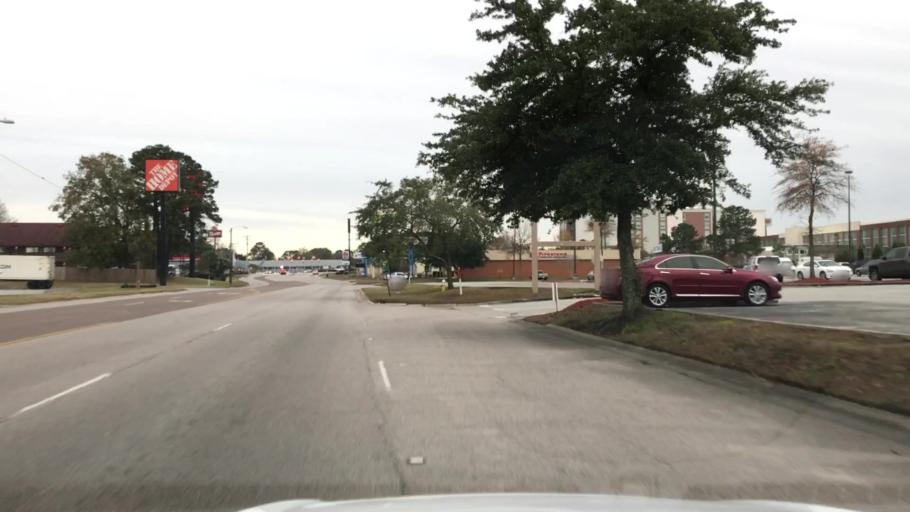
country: US
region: South Carolina
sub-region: Berkeley County
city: Hanahan
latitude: 32.9384
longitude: -80.0462
